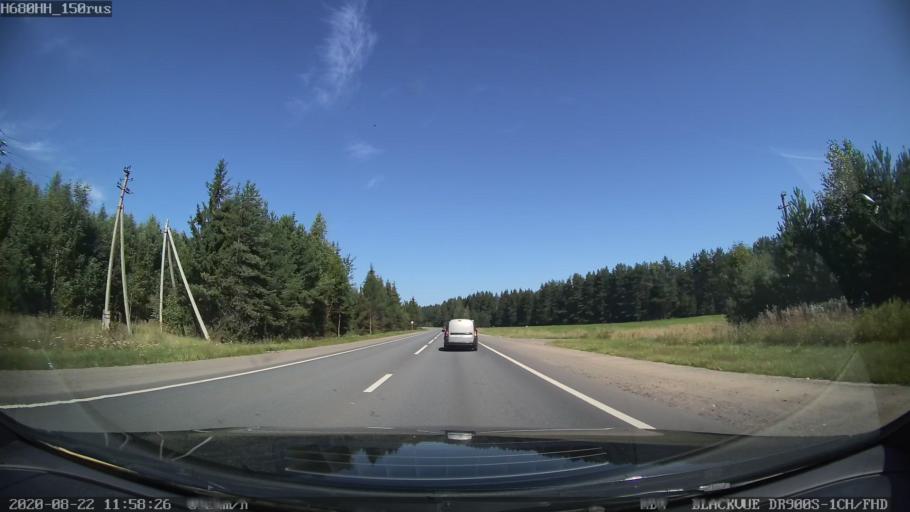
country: RU
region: Tverskaya
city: Rameshki
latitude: 57.1919
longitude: 36.0840
